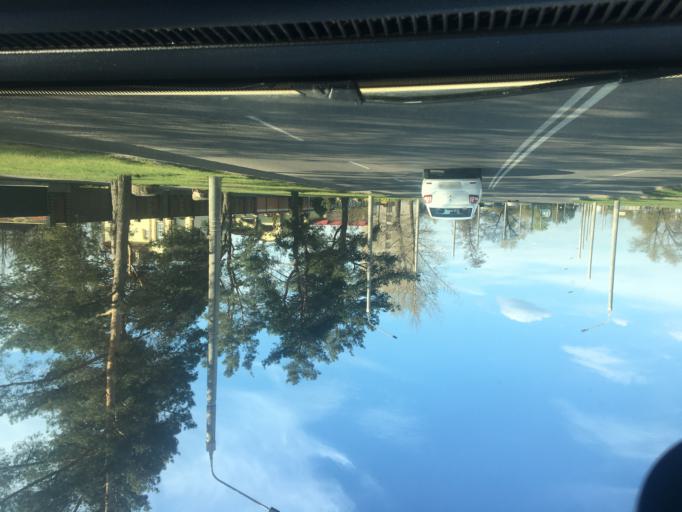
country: BY
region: Mogilev
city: Babruysk
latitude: 53.1601
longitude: 29.1695
